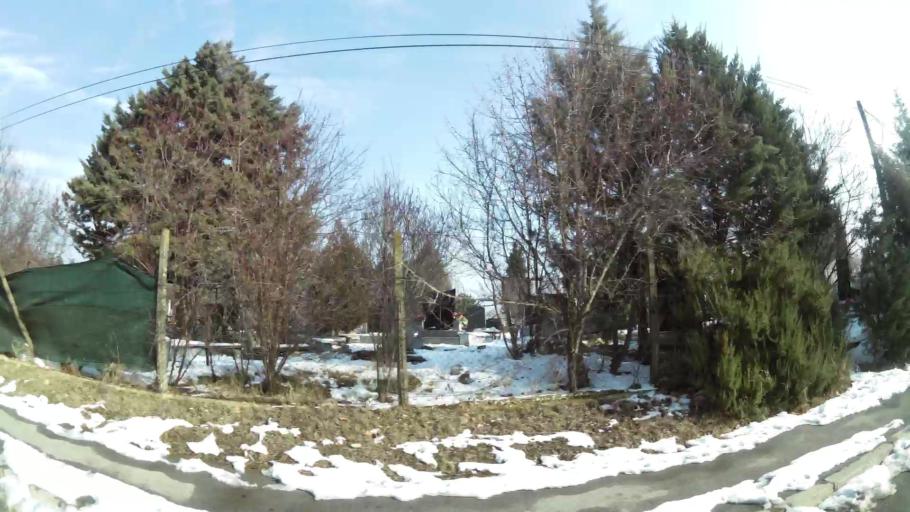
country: MK
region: Suto Orizari
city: Suto Orizare
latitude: 42.0300
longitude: 21.3775
